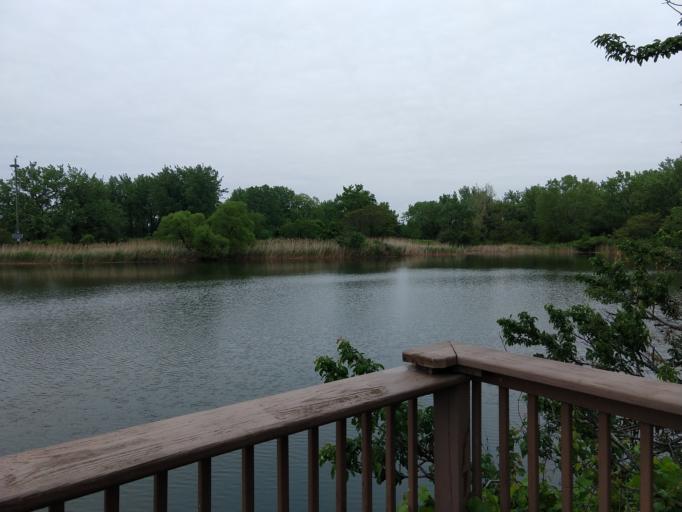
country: US
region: New York
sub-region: Erie County
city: Lackawanna
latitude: 42.8472
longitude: -78.8575
